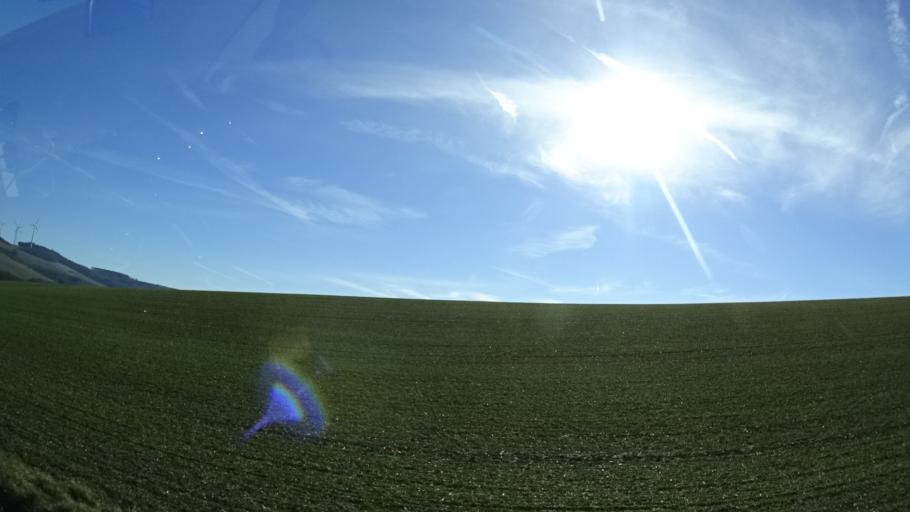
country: DE
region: Rheinland-Pfalz
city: Gerbach
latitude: 49.6735
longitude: 7.8570
